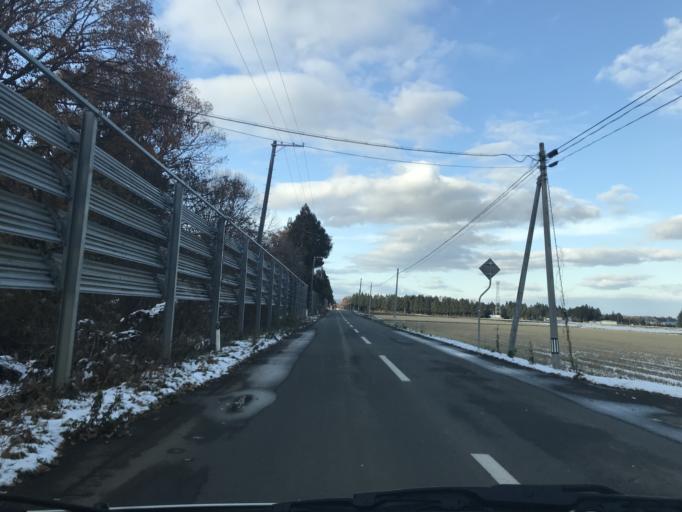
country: JP
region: Iwate
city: Kitakami
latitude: 39.2470
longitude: 141.0326
